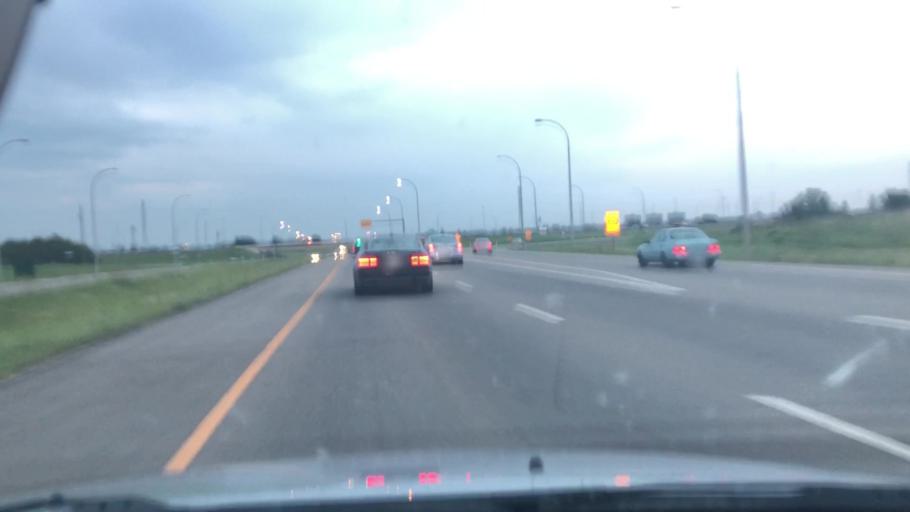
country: CA
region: Alberta
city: St. Albert
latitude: 53.5122
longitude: -113.6669
